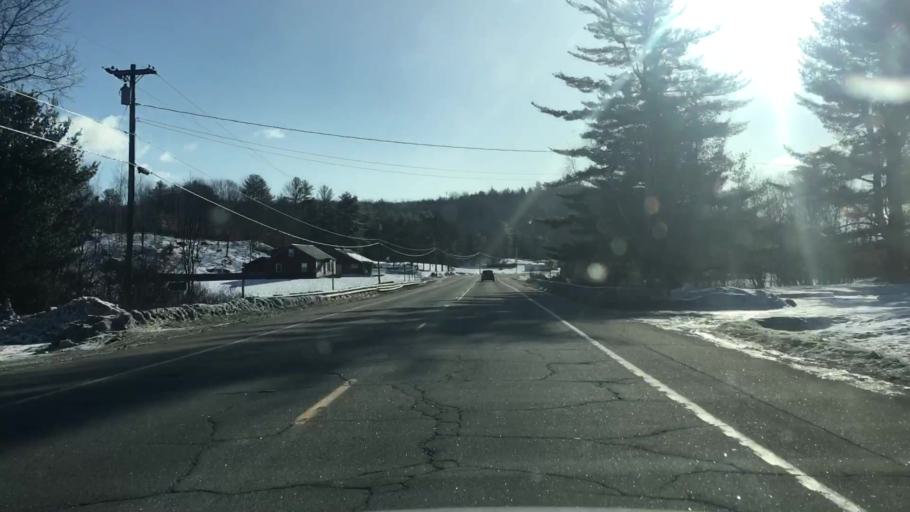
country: US
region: Maine
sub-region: Oxford County
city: West Paris
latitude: 44.3252
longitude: -70.5486
